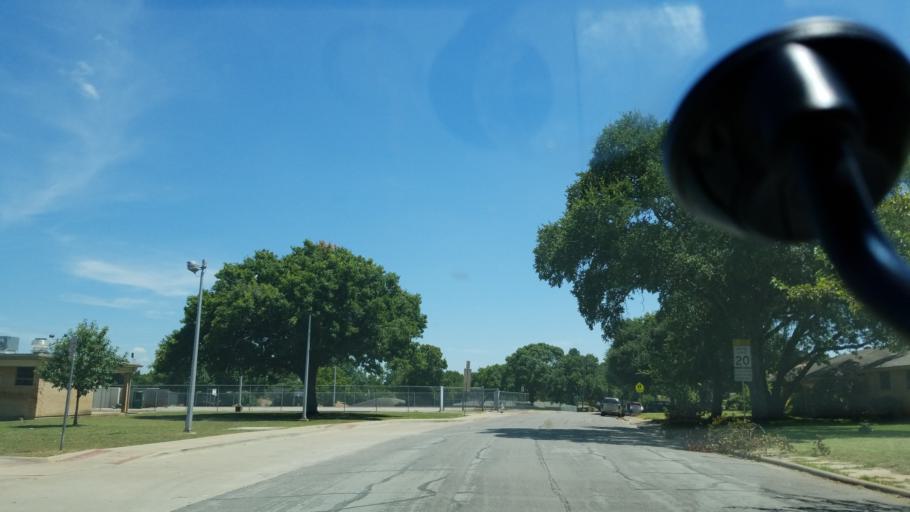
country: US
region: Texas
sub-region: Dallas County
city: Cockrell Hill
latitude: 32.6844
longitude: -96.8347
